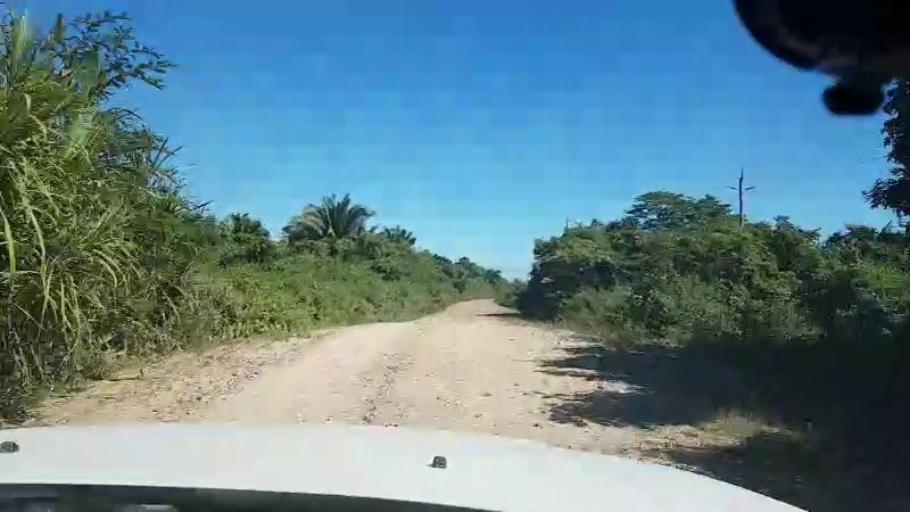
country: BZ
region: Stann Creek
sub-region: Dangriga
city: Dangriga
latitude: 17.1582
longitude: -88.3353
